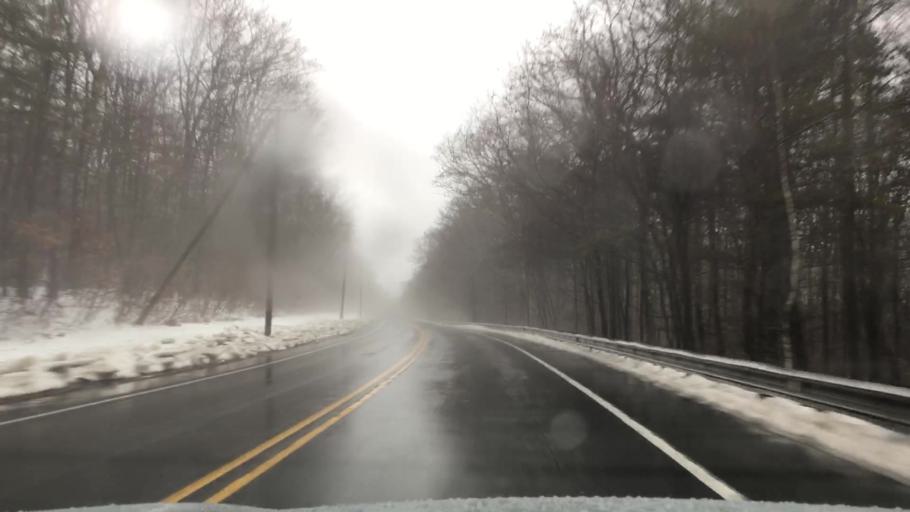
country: US
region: Massachusetts
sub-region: Hampshire County
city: Pelham
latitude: 42.3662
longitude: -72.3984
